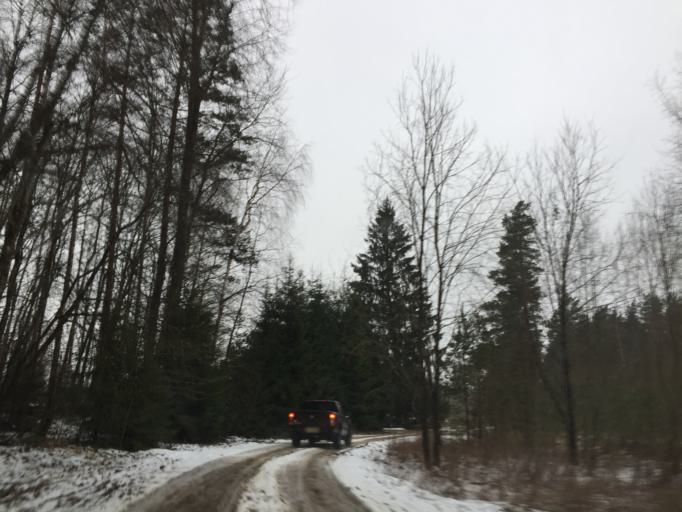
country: LV
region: Seja
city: Loja
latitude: 57.1338
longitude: 24.5907
